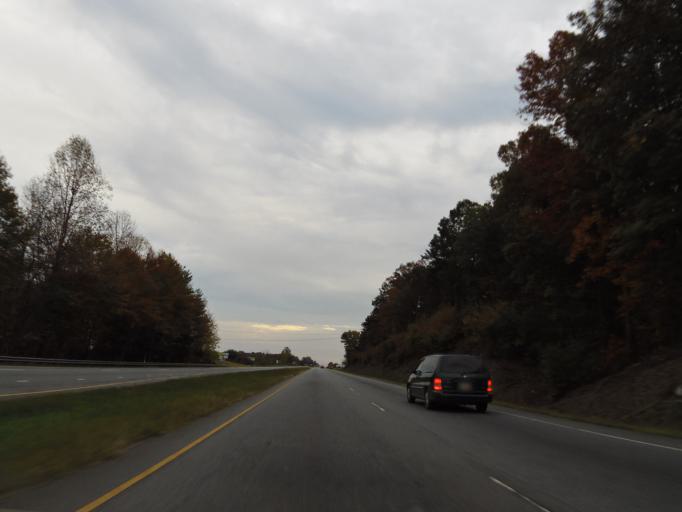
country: US
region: North Carolina
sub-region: Caldwell County
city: Sawmills
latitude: 35.8423
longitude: -81.4690
